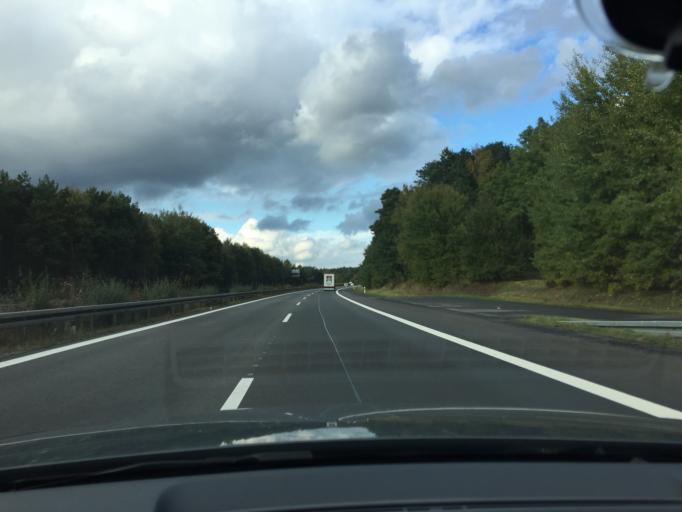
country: DE
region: Brandenburg
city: Bronkow
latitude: 51.6699
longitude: 13.9036
